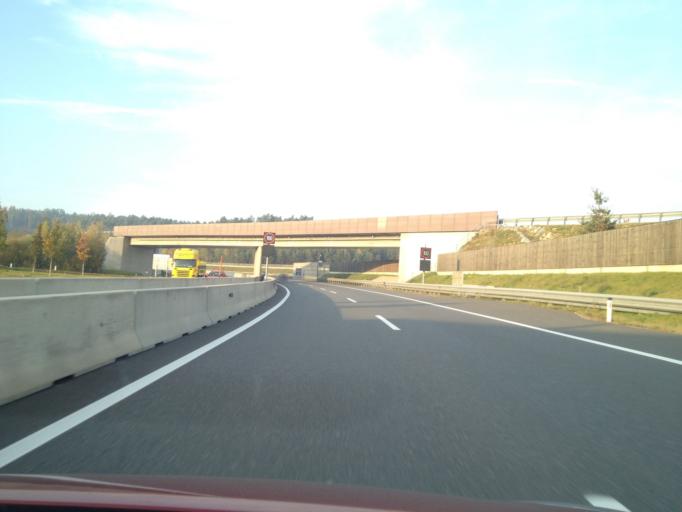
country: AT
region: Upper Austria
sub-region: Politischer Bezirk Urfahr-Umgebung
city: Engerwitzdorf
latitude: 48.3624
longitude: 14.4814
